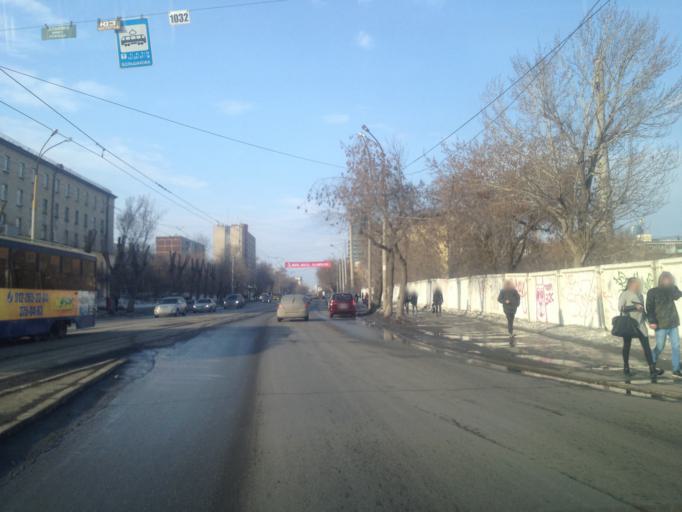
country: RU
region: Sverdlovsk
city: Yekaterinburg
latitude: 56.8186
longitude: 60.6065
